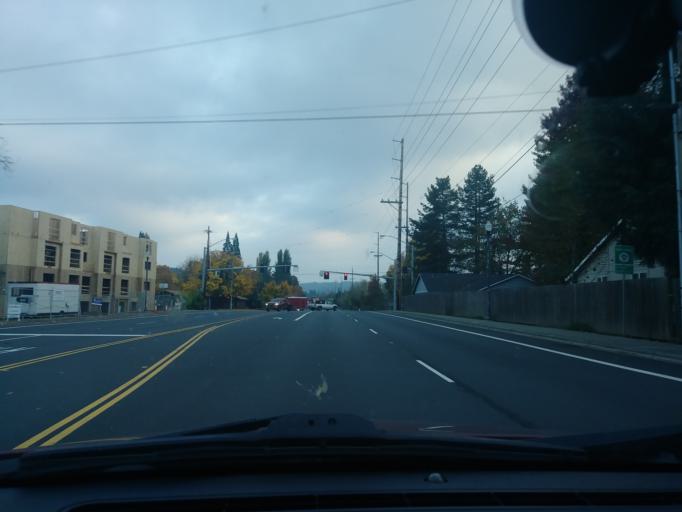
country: US
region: Oregon
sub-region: Washington County
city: Aloha
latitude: 45.4914
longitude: -122.8520
